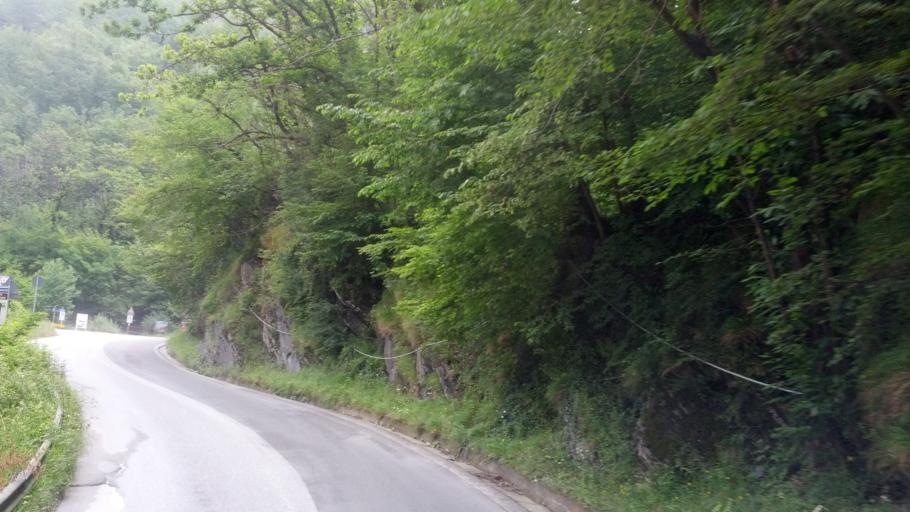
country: IT
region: Tuscany
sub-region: Provincia di Massa-Carrara
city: Massa
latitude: 44.0793
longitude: 10.1408
